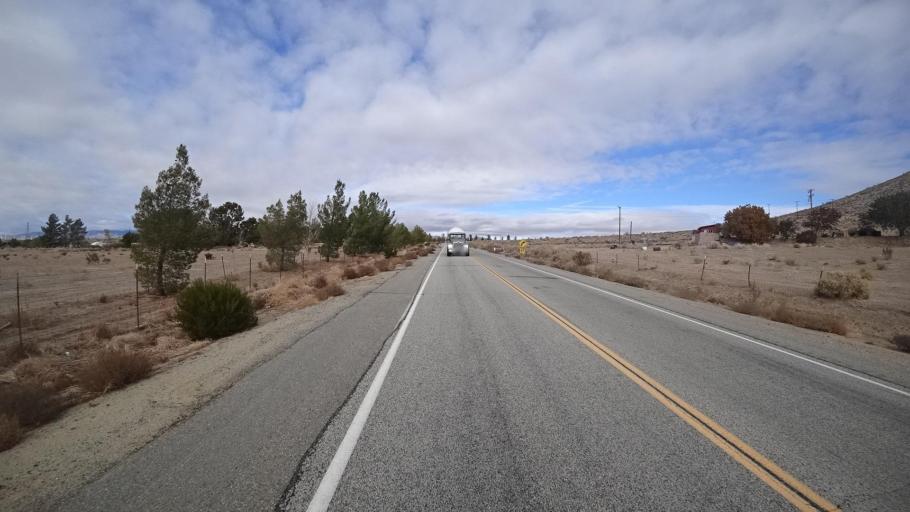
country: US
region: California
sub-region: Kern County
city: Rosamond
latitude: 34.8773
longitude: -118.2923
